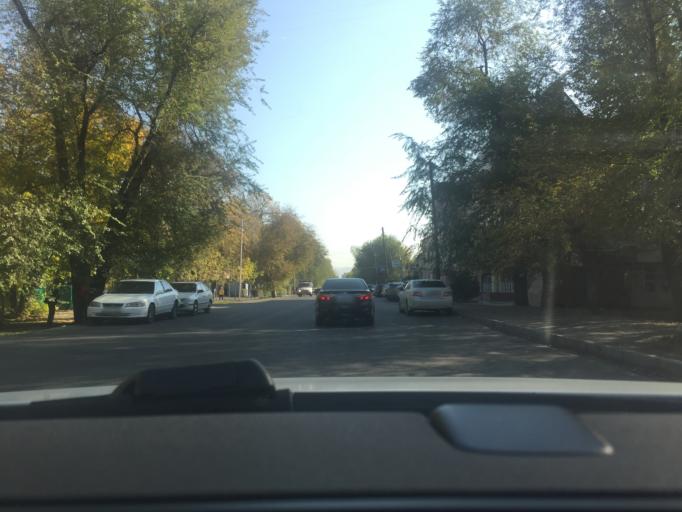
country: KZ
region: Almaty Qalasy
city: Almaty
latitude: 43.2485
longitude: 76.9039
